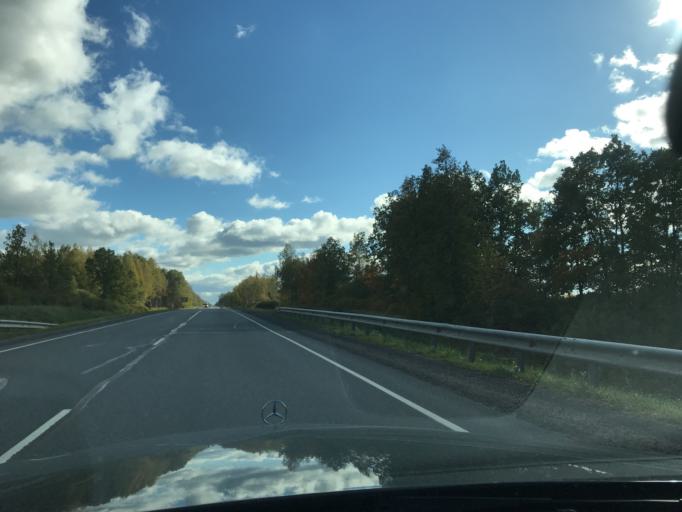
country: RU
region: Pskov
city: Ostrov
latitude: 57.2219
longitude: 28.4466
